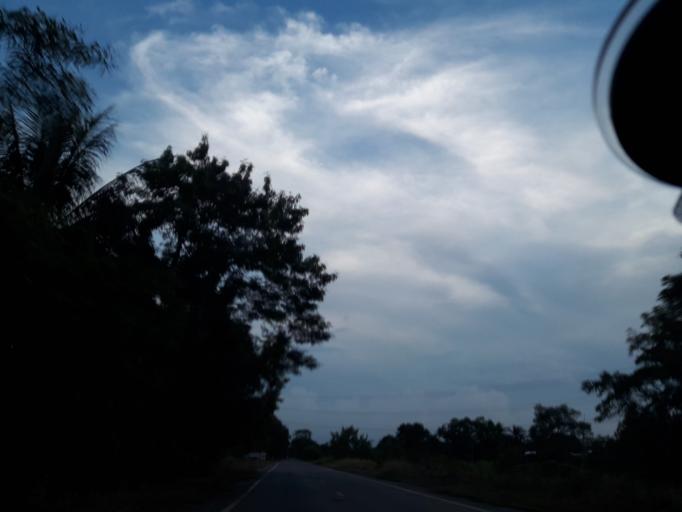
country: TH
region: Pathum Thani
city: Nong Suea
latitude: 14.1884
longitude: 100.8689
